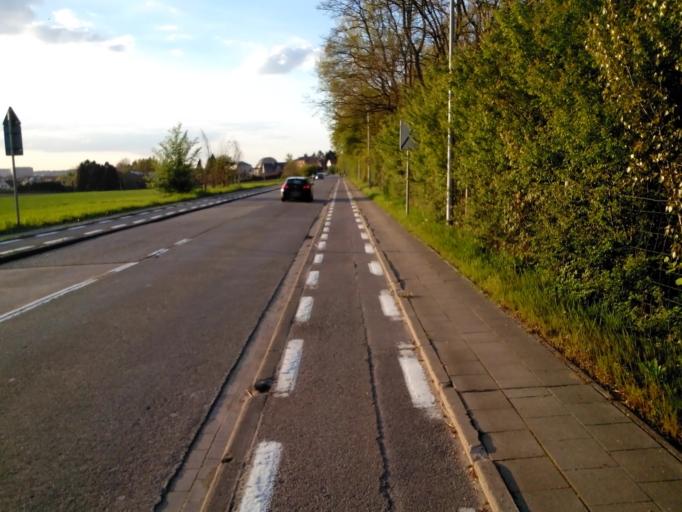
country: BE
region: Flanders
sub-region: Provincie Vlaams-Brabant
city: Leuven
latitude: 50.8558
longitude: 4.7196
